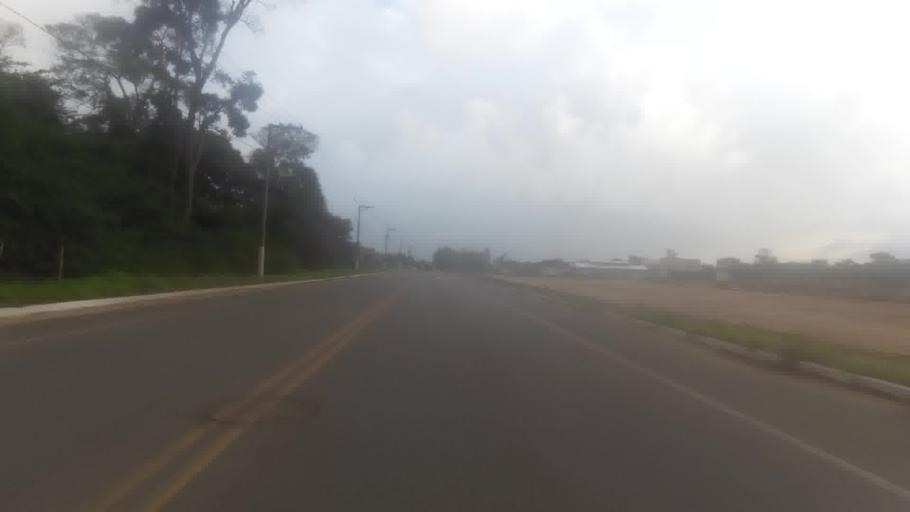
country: BR
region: Espirito Santo
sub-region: Piuma
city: Piuma
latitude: -20.8034
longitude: -40.6341
